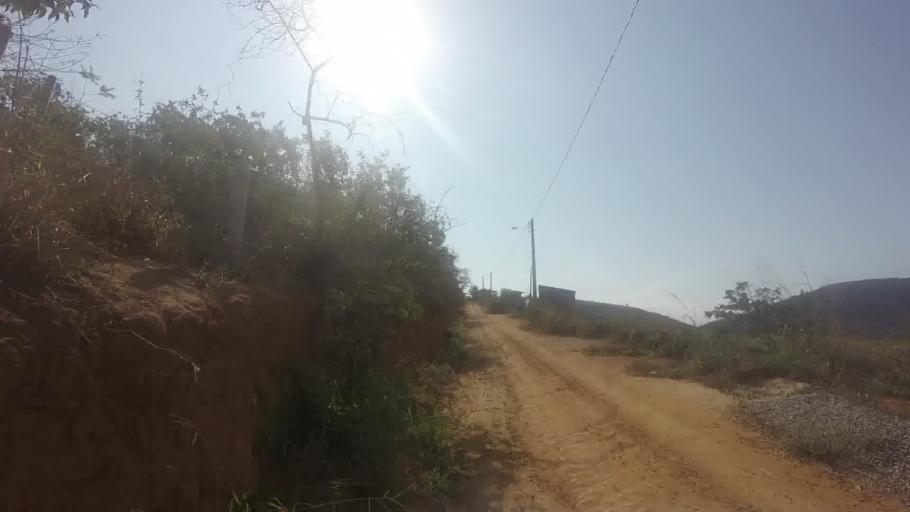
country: BR
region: Espirito Santo
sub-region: Piuma
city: Piuma
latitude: -20.8869
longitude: -40.7720
